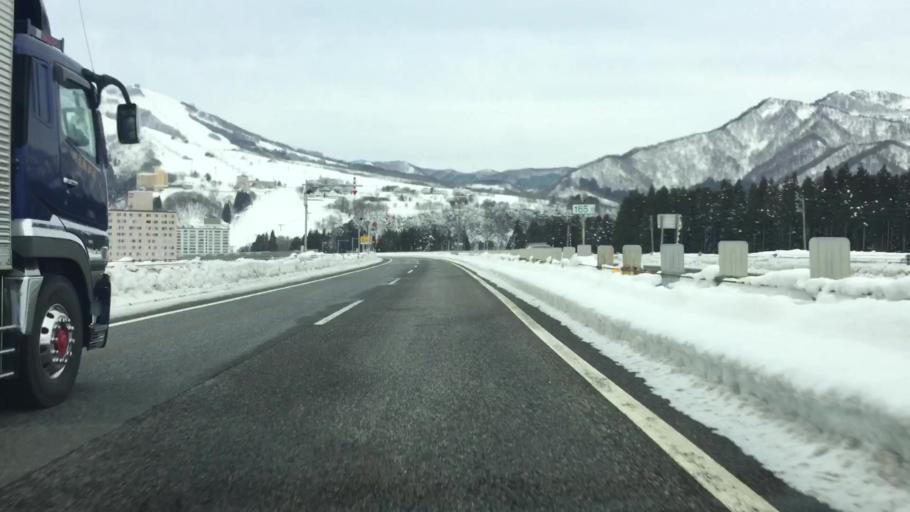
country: JP
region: Niigata
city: Shiozawa
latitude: 36.9209
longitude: 138.8409
